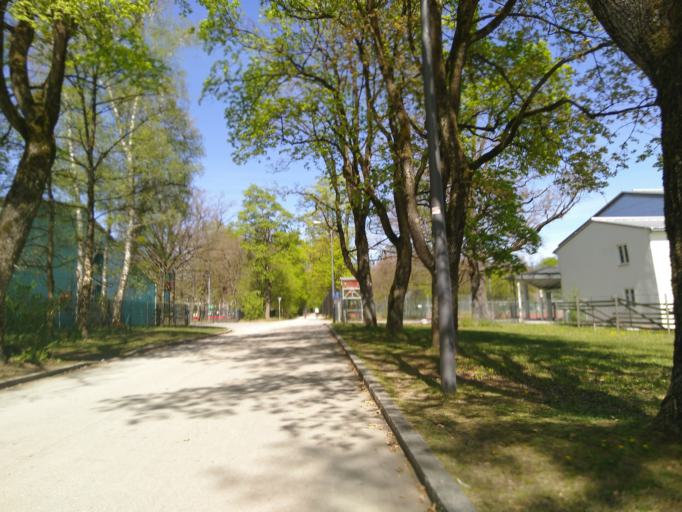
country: DE
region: Bavaria
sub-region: Upper Bavaria
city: Unterhaching
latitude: 48.0932
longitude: 11.6025
